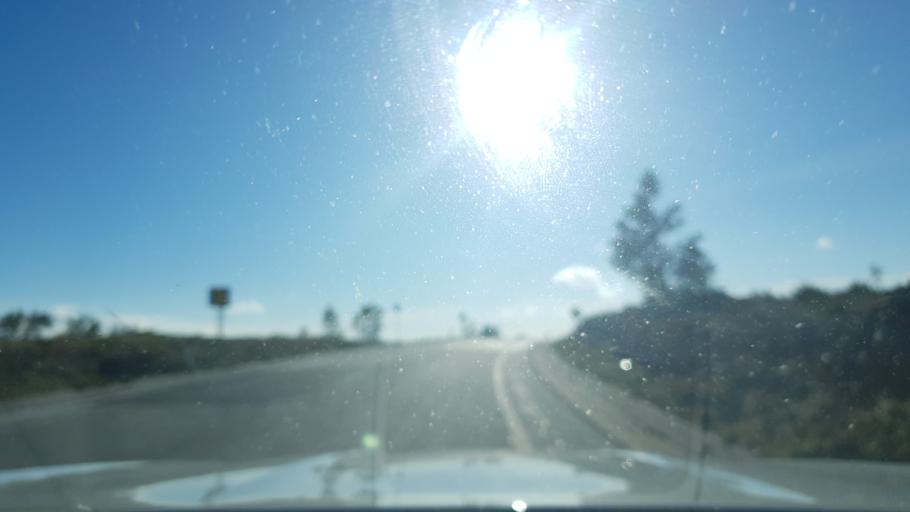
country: PT
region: Braganca
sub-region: Freixo de Espada A Cinta
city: Freixo de Espada a Cinta
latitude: 41.1522
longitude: -6.8007
